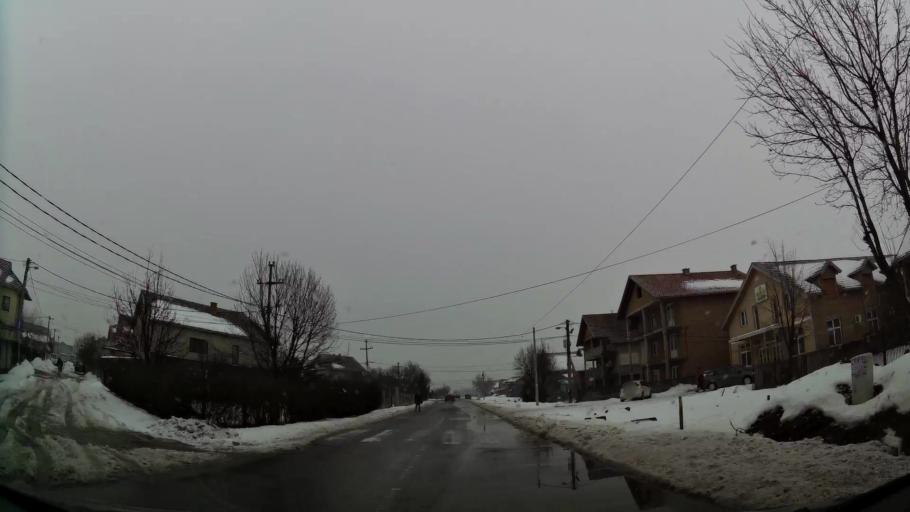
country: RS
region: Central Serbia
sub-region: Belgrade
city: Zemun
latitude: 44.8578
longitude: 20.3295
